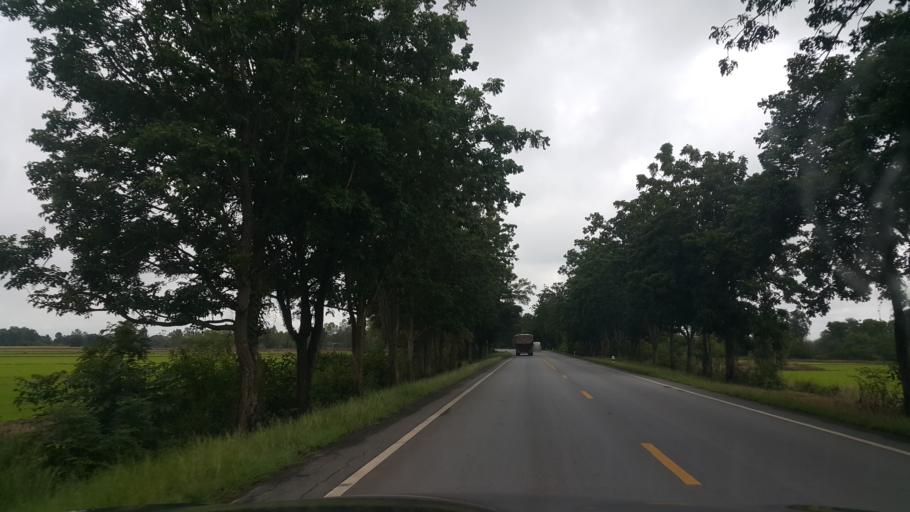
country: TH
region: Sukhothai
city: Sawankhalok
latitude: 17.3389
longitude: 99.7423
